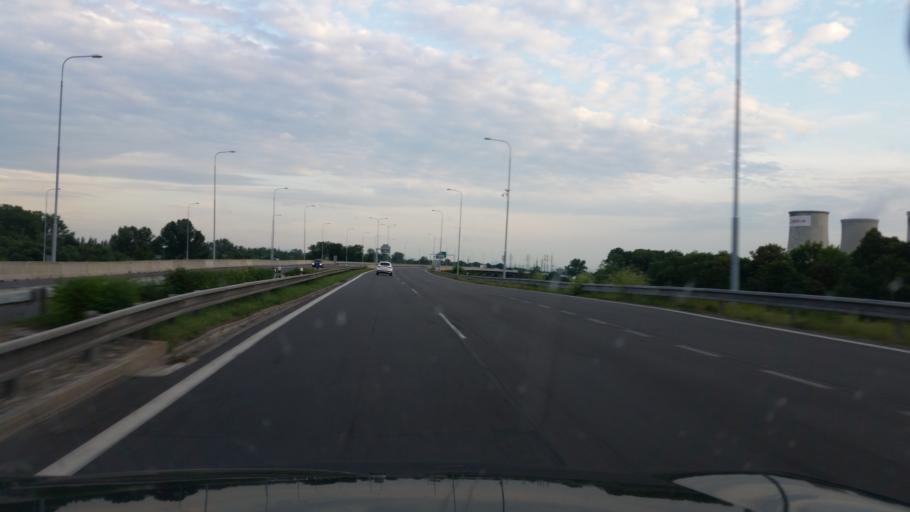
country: CZ
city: Ludgerovice
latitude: 49.8352
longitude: 18.2186
